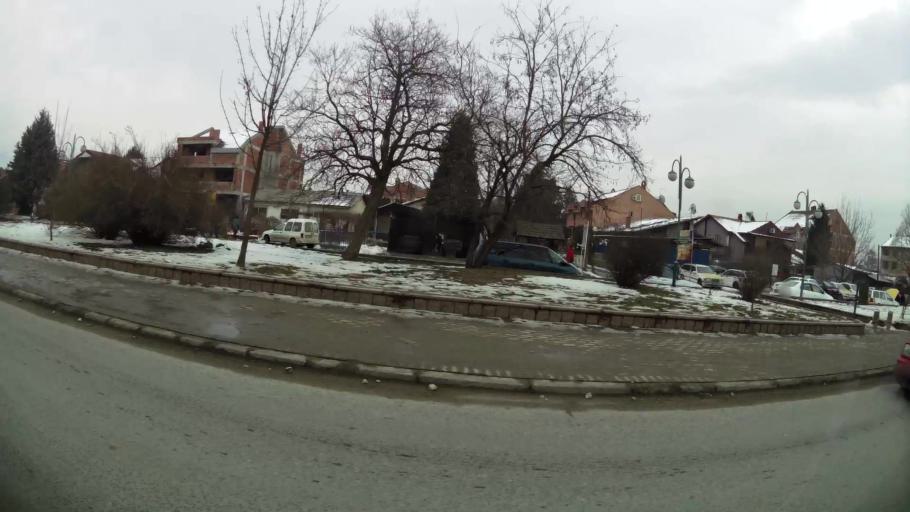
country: MK
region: Butel
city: Butel
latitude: 42.0294
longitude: 21.4447
